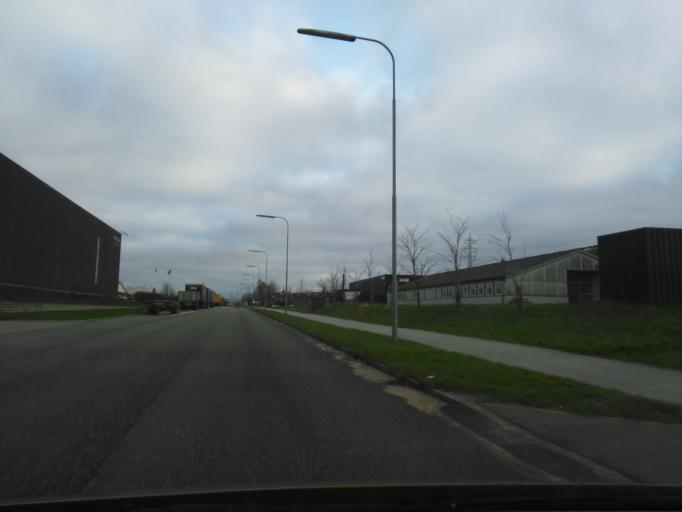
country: DK
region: Central Jutland
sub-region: Arhus Kommune
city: Stavtrup
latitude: 56.1677
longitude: 10.1034
